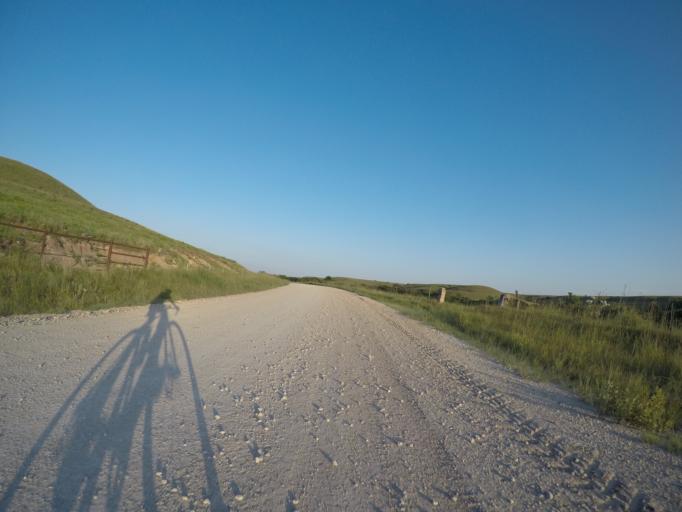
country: US
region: Kansas
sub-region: Riley County
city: Ogden
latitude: 39.0144
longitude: -96.6659
